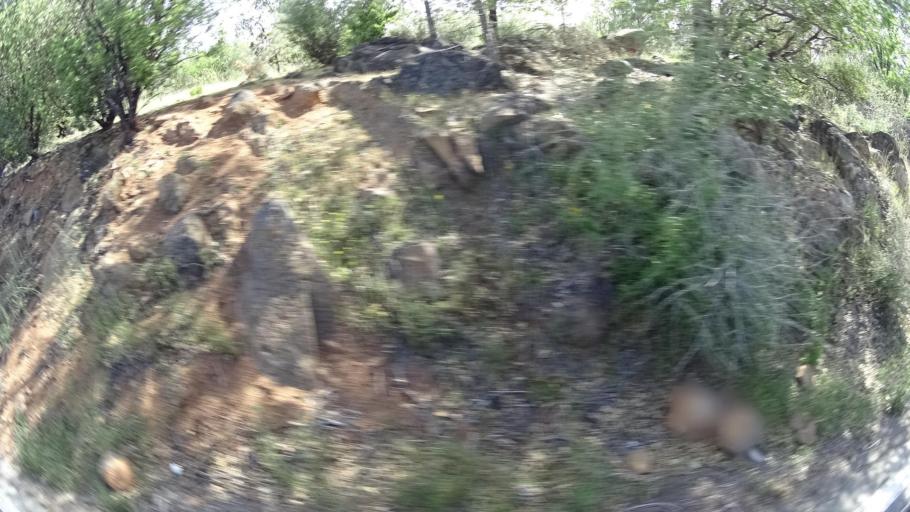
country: US
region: California
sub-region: Lake County
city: Cobb
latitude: 38.8801
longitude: -122.7817
